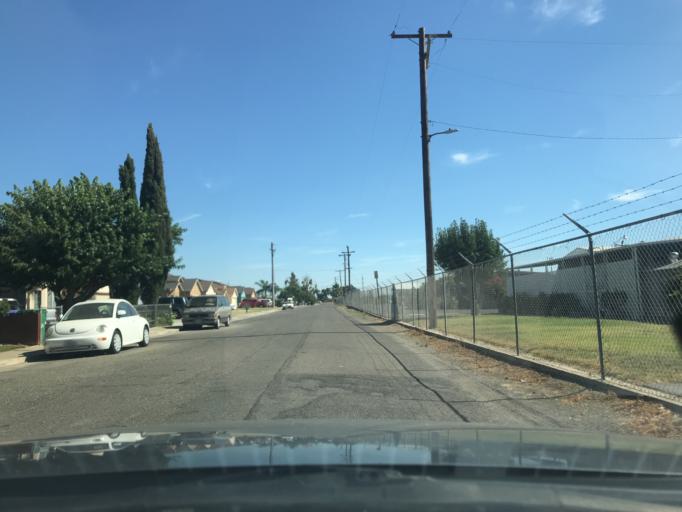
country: US
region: California
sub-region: Merced County
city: Merced
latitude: 37.3202
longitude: -120.5296
